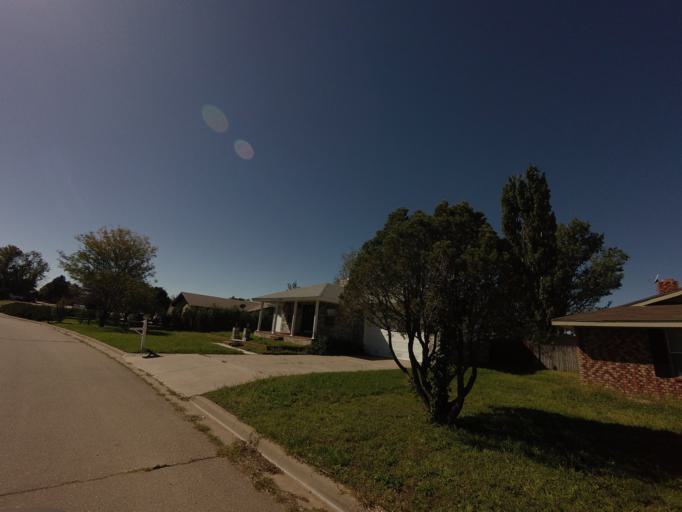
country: US
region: New Mexico
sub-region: Curry County
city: Clovis
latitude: 34.4247
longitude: -103.1893
